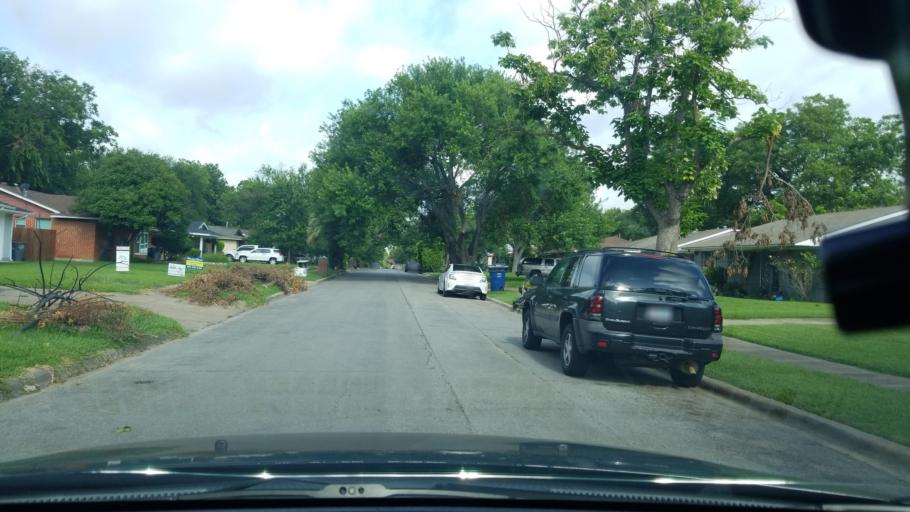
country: US
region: Texas
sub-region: Dallas County
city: Mesquite
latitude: 32.8169
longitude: -96.6695
